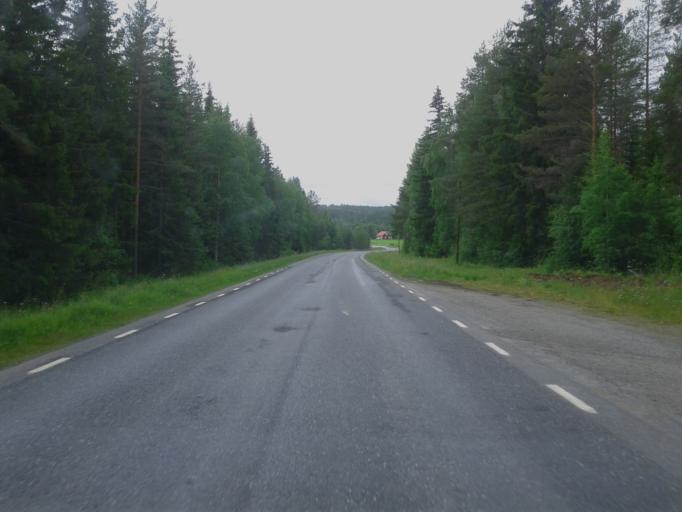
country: SE
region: Vaesterbotten
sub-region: Skelleftea Kommun
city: Forsbacka
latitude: 64.9073
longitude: 20.5985
